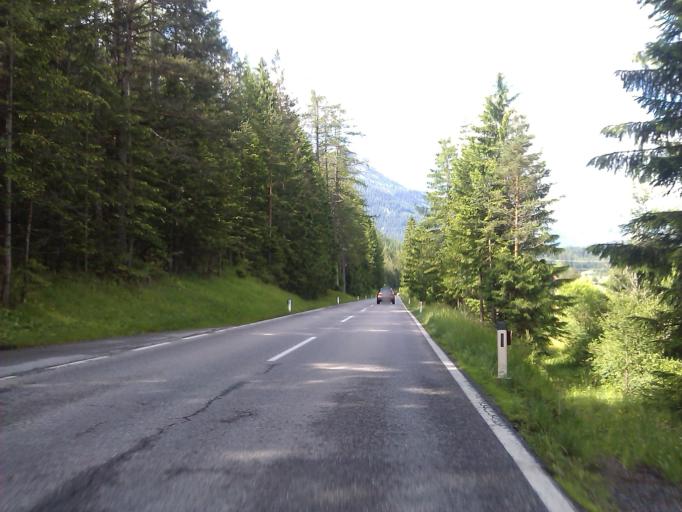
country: AT
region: Tyrol
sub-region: Politischer Bezirk Reutte
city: Biberwier
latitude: 47.3881
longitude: 10.9113
